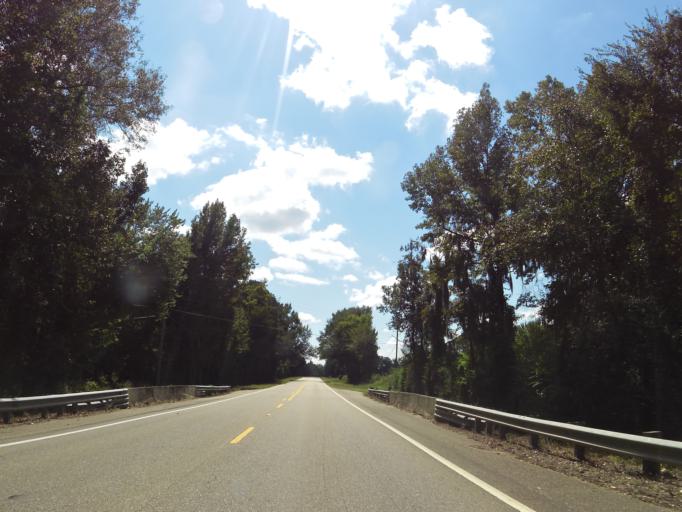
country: US
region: Alabama
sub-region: Dallas County
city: Selma
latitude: 32.4728
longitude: -87.0926
